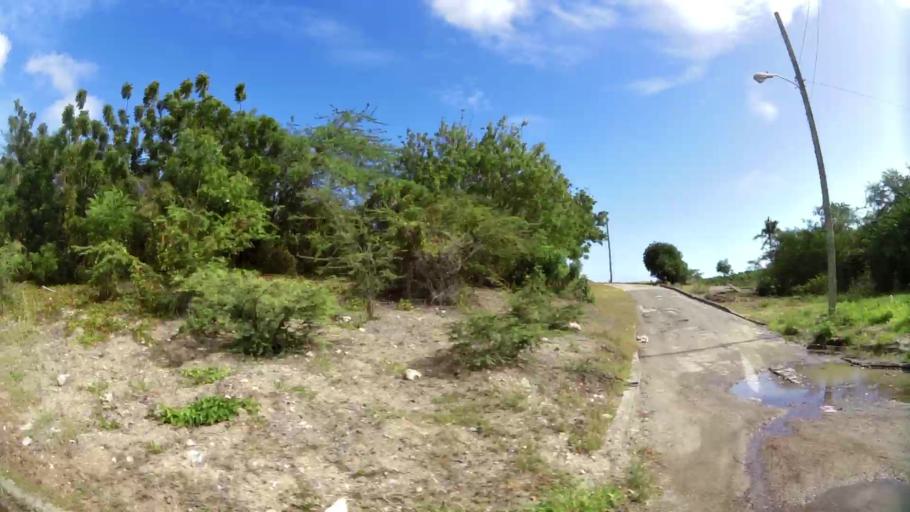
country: AG
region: Saint Paul
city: Liberta
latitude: 17.0417
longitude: -61.7509
